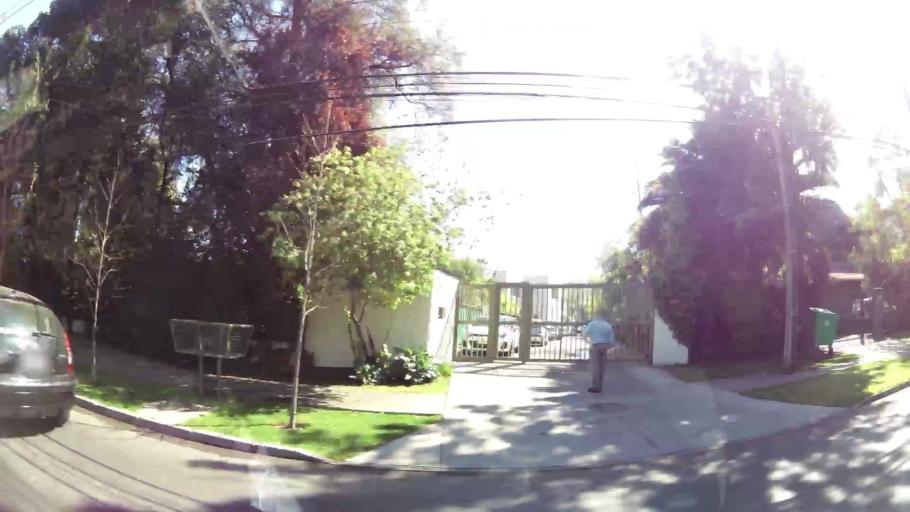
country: CL
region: Santiago Metropolitan
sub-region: Provincia de Santiago
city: Villa Presidente Frei, Nunoa, Santiago, Chile
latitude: -33.4420
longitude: -70.5516
